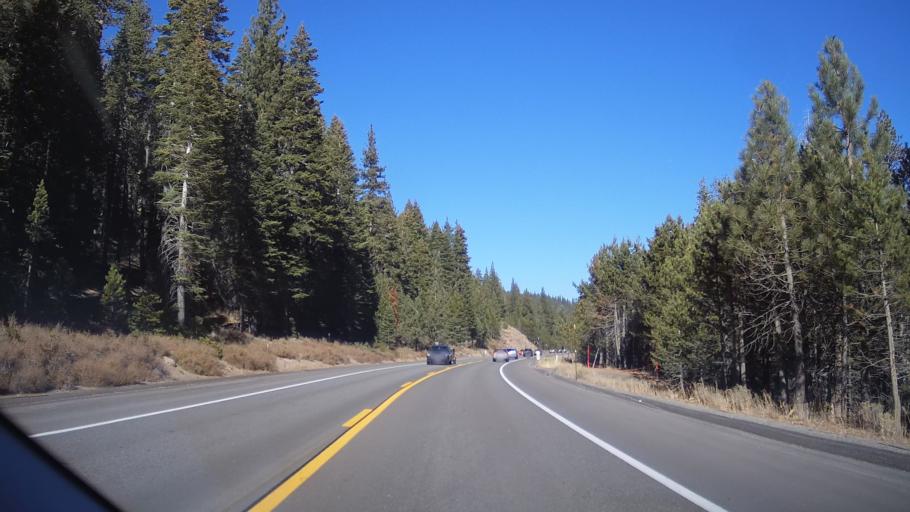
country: US
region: California
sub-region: Nevada County
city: Truckee
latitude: 39.2442
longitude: -120.2106
